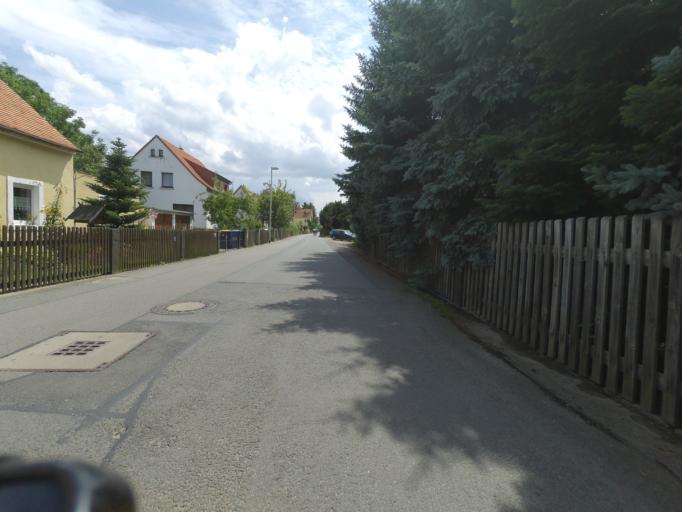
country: DE
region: Saxony
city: Heidenau
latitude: 50.9955
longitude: 13.8811
